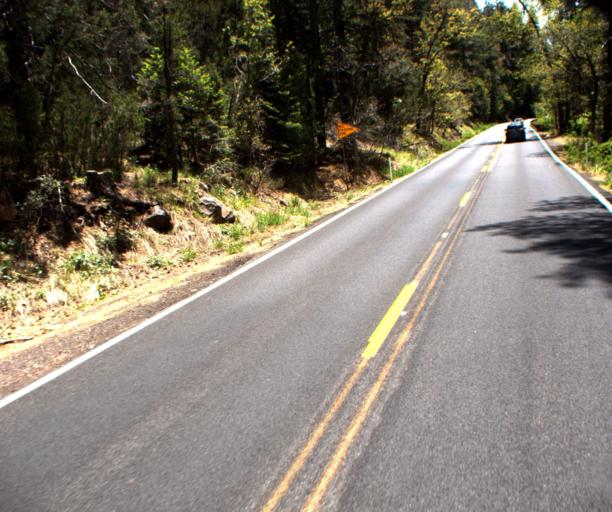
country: US
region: Arizona
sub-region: Coconino County
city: Kachina Village
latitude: 35.0171
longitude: -111.7373
